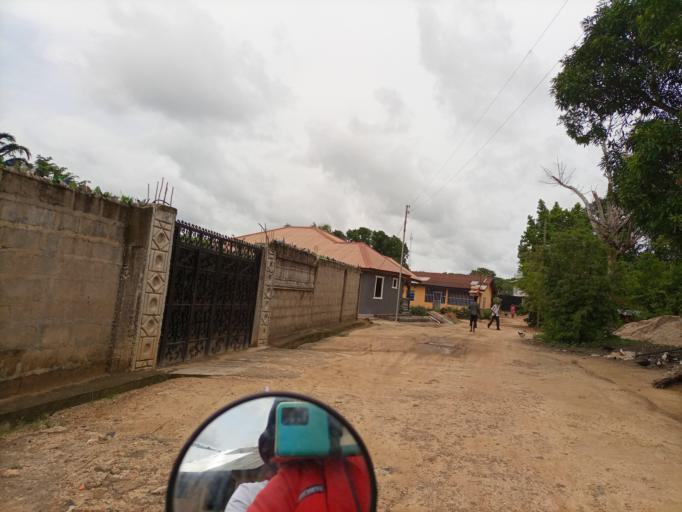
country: SL
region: Southern Province
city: Bo
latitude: 7.9493
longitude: -11.7474
